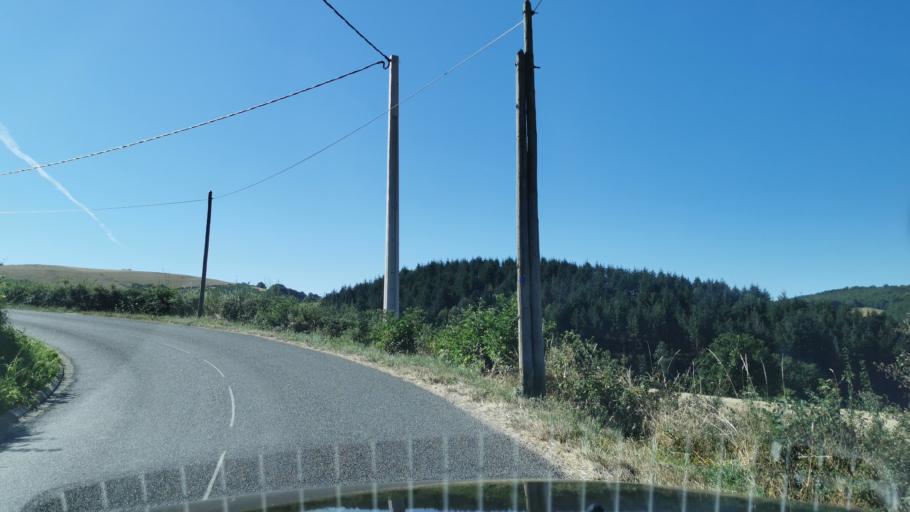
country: FR
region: Bourgogne
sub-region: Departement de Saone-et-Loire
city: Marmagne
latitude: 46.8054
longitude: 4.3357
